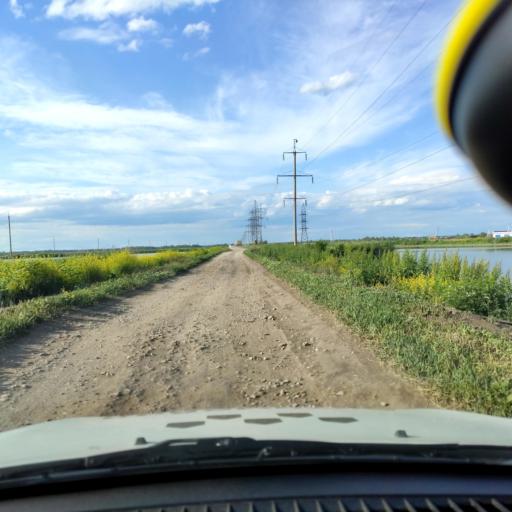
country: RU
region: Samara
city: Tol'yatti
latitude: 53.5927
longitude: 49.4367
